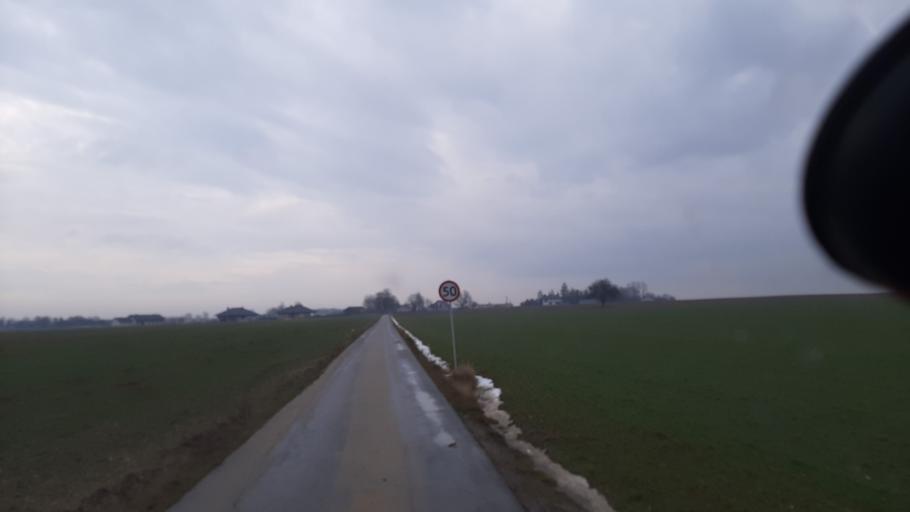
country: PL
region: Lublin Voivodeship
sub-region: Powiat lubelski
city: Jastkow
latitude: 51.3444
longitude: 22.5023
